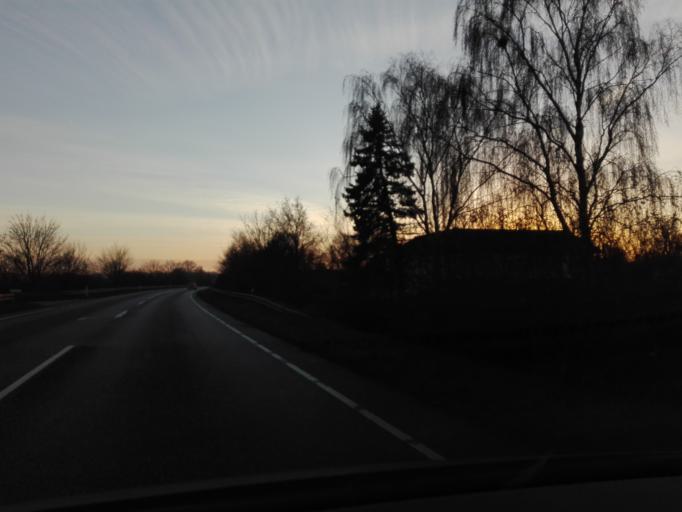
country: DK
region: Central Jutland
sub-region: Arhus Kommune
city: Framlev
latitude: 56.1468
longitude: 10.0063
